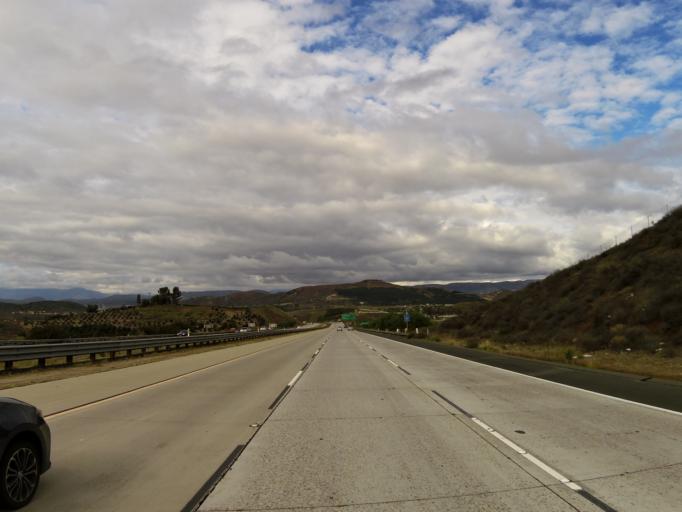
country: US
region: California
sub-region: Ventura County
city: Moorpark
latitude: 34.2485
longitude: -118.8397
